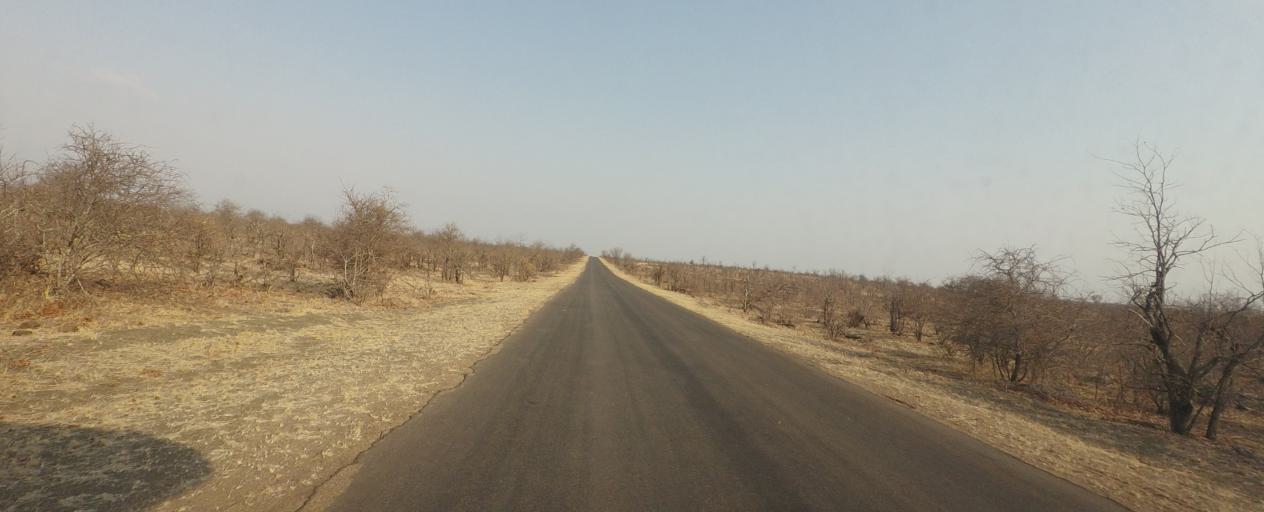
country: ZA
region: Limpopo
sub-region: Mopani District Municipality
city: Giyani
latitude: -23.0821
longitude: 31.4176
